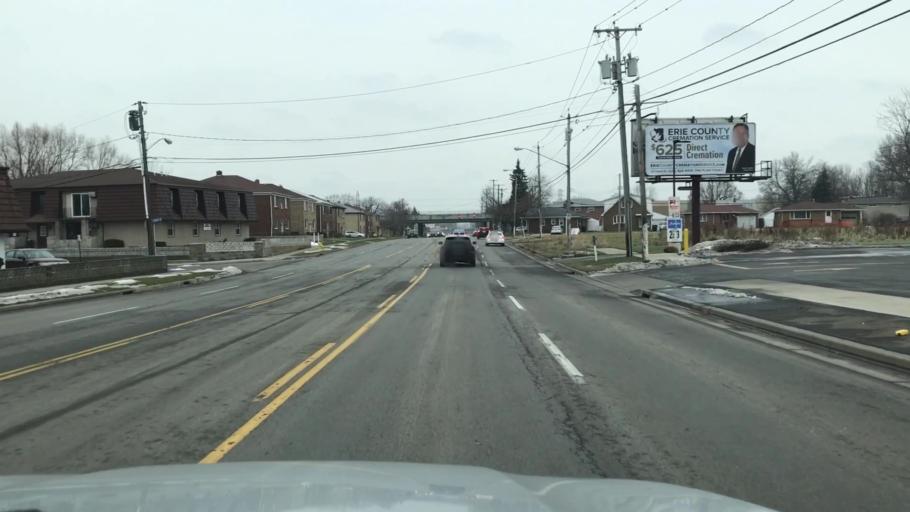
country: US
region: New York
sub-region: Erie County
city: Blasdell
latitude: 42.8086
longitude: -78.7985
